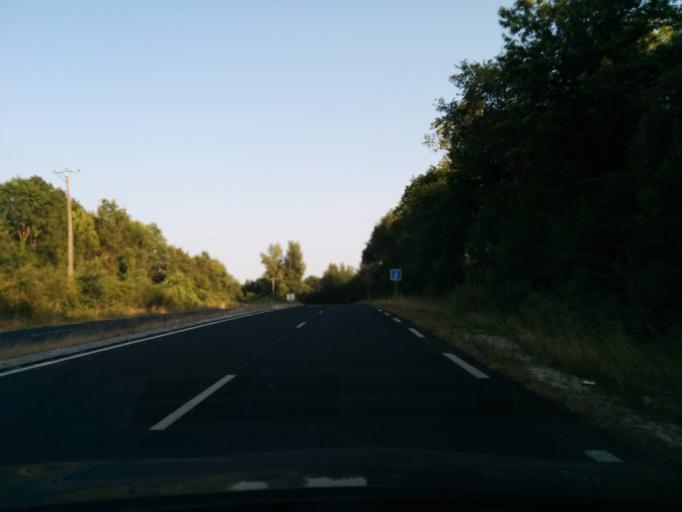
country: FR
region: Midi-Pyrenees
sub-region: Departement du Lot
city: Le Vigan
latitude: 44.7627
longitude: 1.4851
